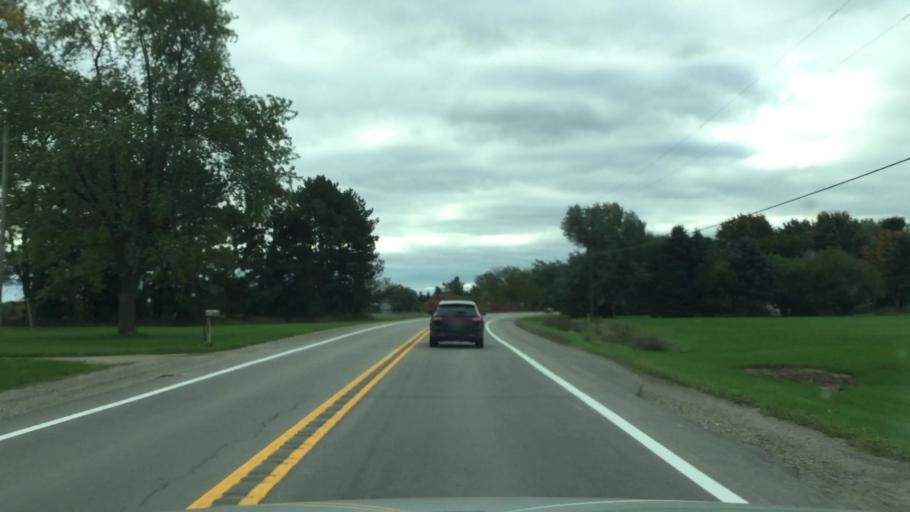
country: US
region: Michigan
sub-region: Macomb County
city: Memphis
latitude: 42.8563
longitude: -82.7648
